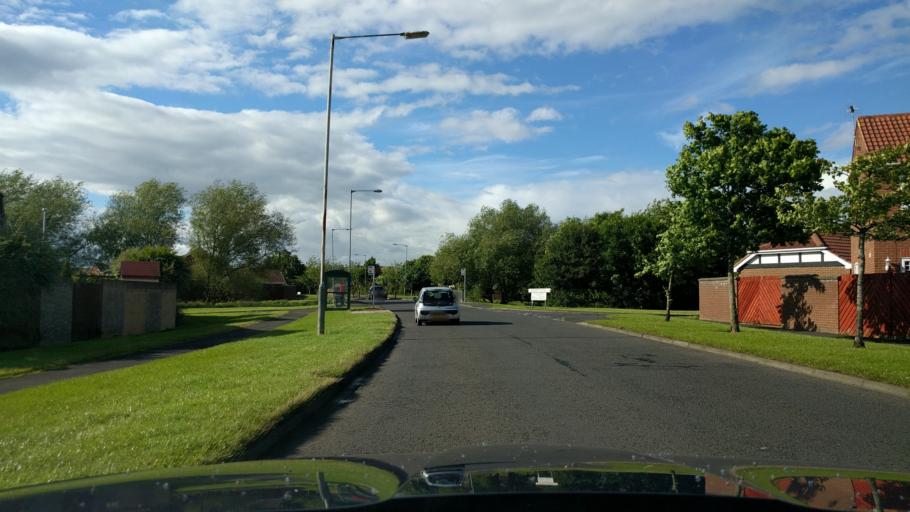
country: GB
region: England
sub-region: Northumberland
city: Cramlington
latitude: 55.0998
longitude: -1.5769
